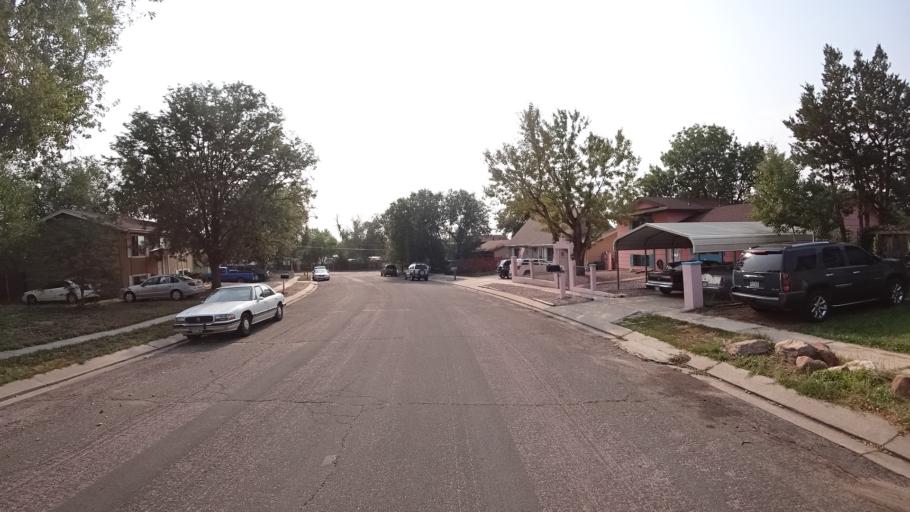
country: US
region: Colorado
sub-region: El Paso County
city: Stratmoor
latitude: 38.7997
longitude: -104.7650
